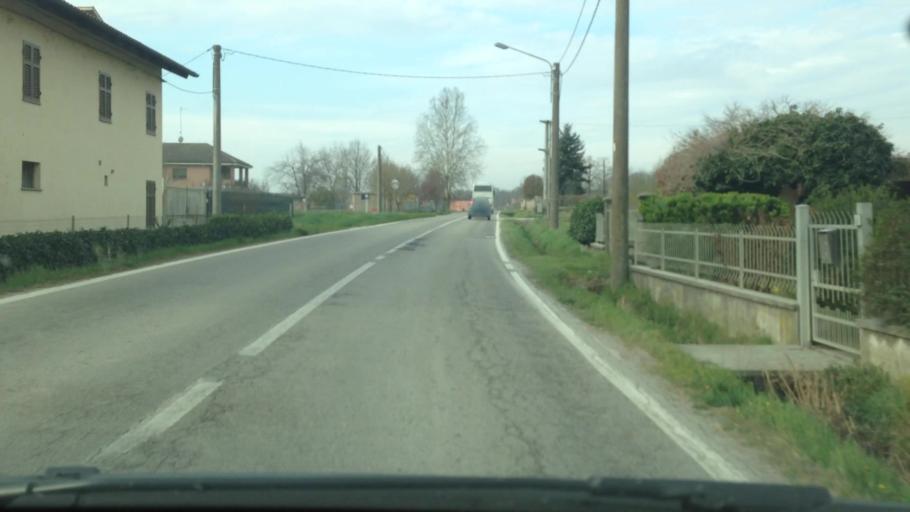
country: IT
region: Piedmont
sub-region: Provincia di Asti
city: Celle Enomondo
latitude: 44.8692
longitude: 8.1112
